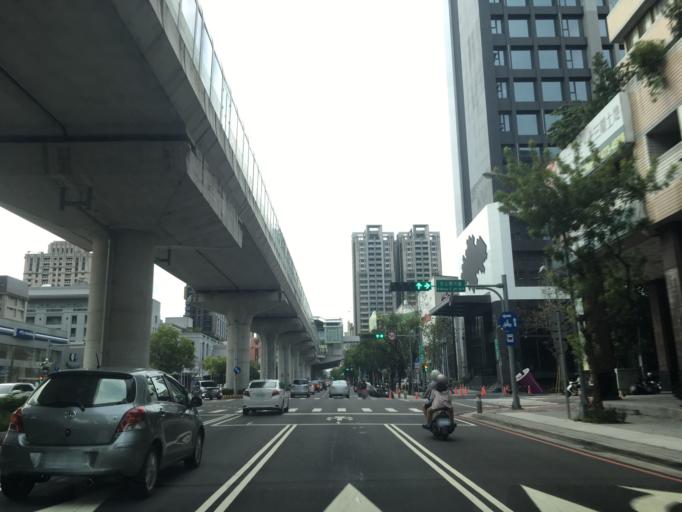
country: TW
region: Taiwan
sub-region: Taichung City
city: Taichung
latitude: 24.1308
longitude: 120.6465
